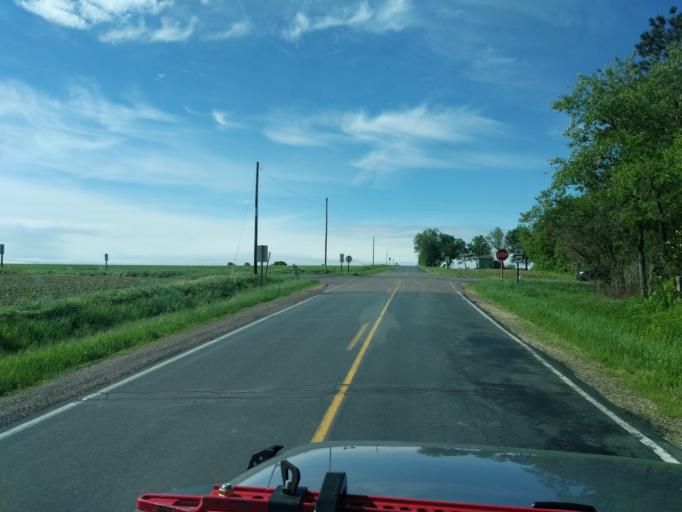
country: US
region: Wisconsin
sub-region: Saint Croix County
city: Hammond
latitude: 44.8703
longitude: -92.4970
